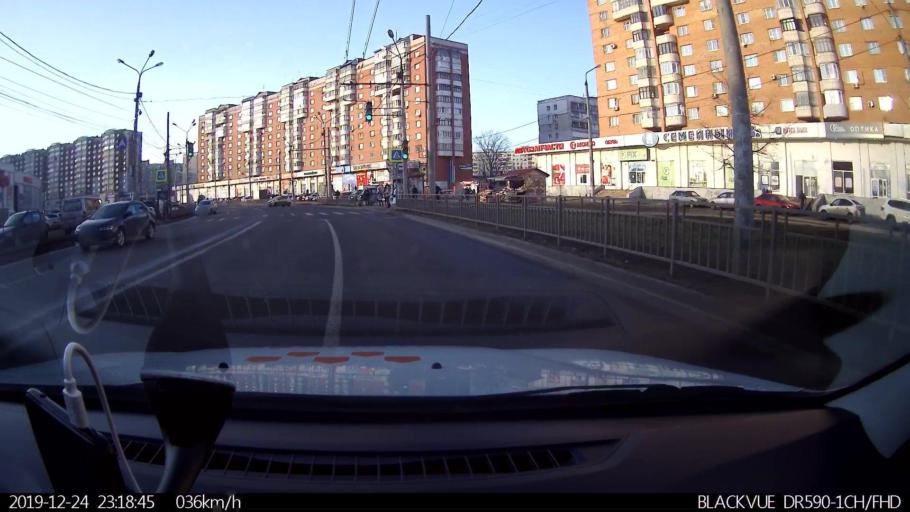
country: RU
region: Nizjnij Novgorod
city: Gorbatovka
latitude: 56.2605
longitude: 43.8559
